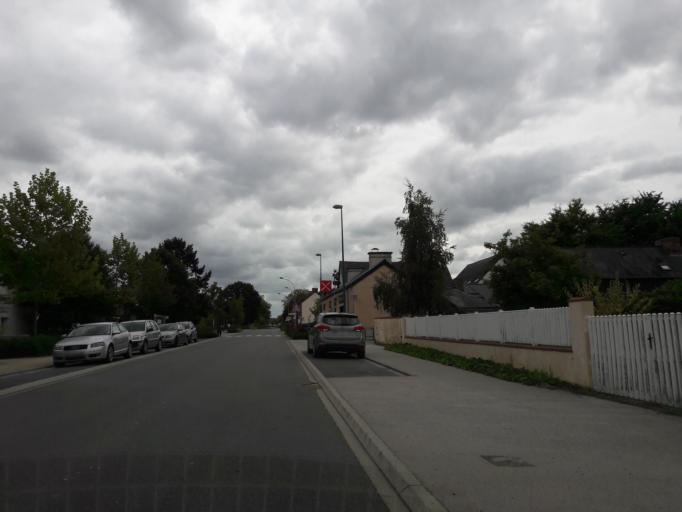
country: FR
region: Brittany
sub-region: Departement d'Ille-et-Vilaine
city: Chartres-de-Bretagne
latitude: 48.0144
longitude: -1.7032
